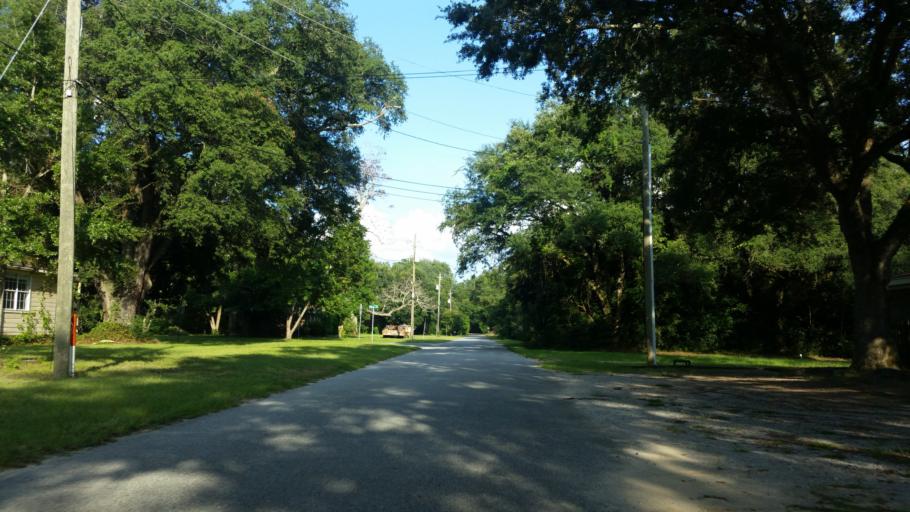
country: US
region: Florida
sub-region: Escambia County
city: Ferry Pass
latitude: 30.4833
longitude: -87.1965
